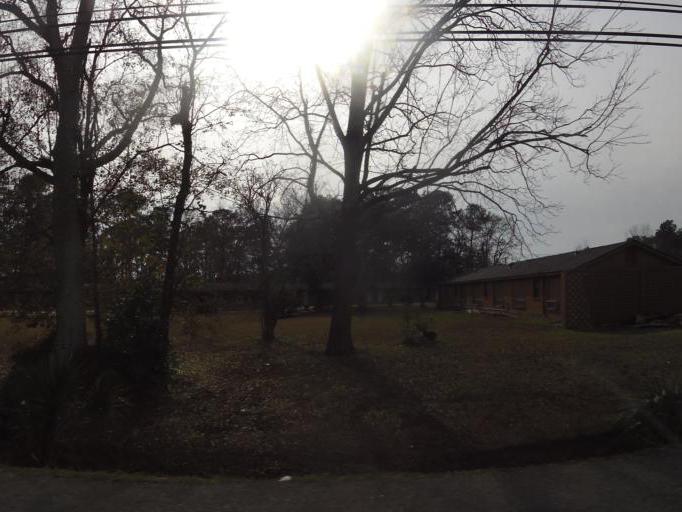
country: US
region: Alabama
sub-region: Houston County
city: Cowarts
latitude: 31.2036
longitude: -85.3466
